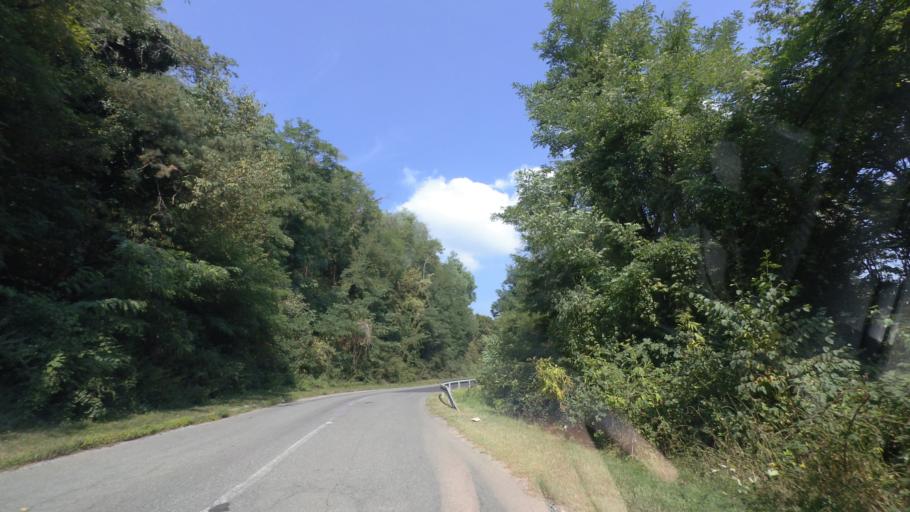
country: BA
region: Federation of Bosnia and Herzegovina
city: Zboriste
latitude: 45.1530
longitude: 16.1534
